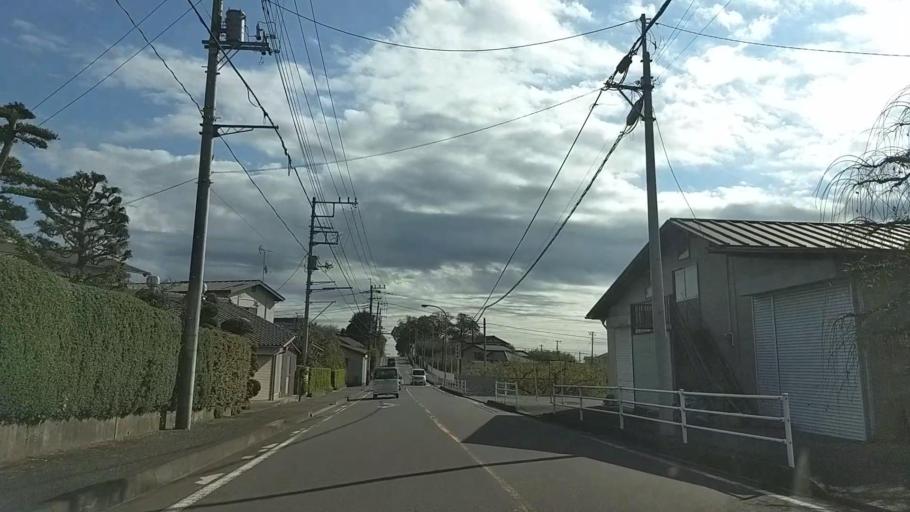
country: JP
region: Kanagawa
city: Odawara
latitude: 35.2988
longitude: 139.1961
